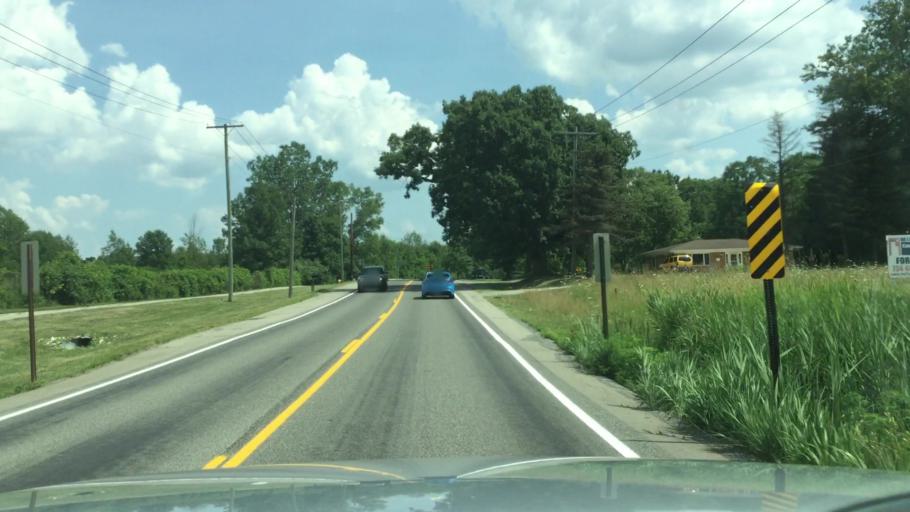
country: US
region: Michigan
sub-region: Washtenaw County
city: Ypsilanti
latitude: 42.2049
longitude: -83.6117
